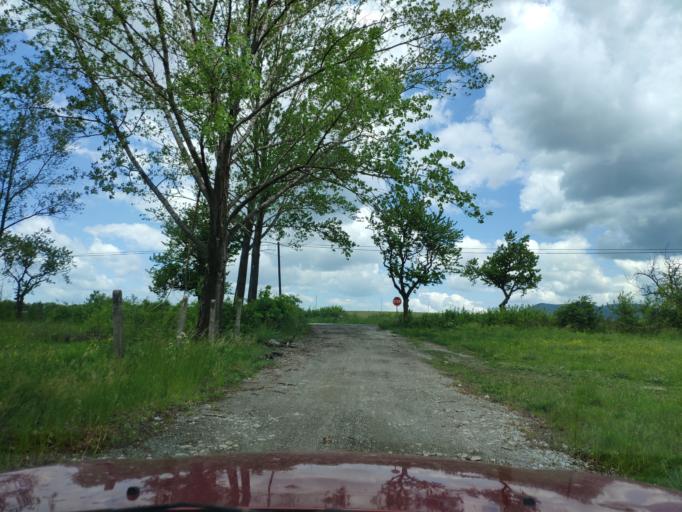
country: SK
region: Kosicky
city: Kosice
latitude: 48.8458
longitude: 21.3251
